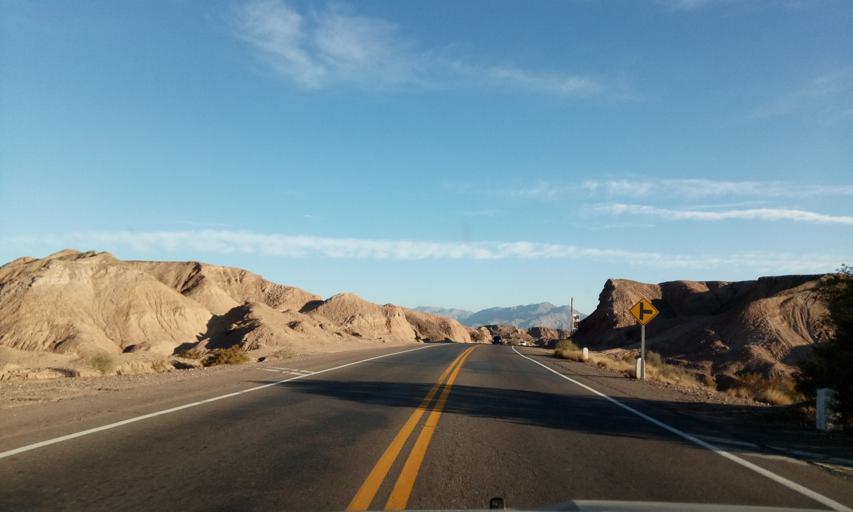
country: AR
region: San Juan
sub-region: Departamento de Rivadavia
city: Rivadavia
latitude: -31.4557
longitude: -68.6377
